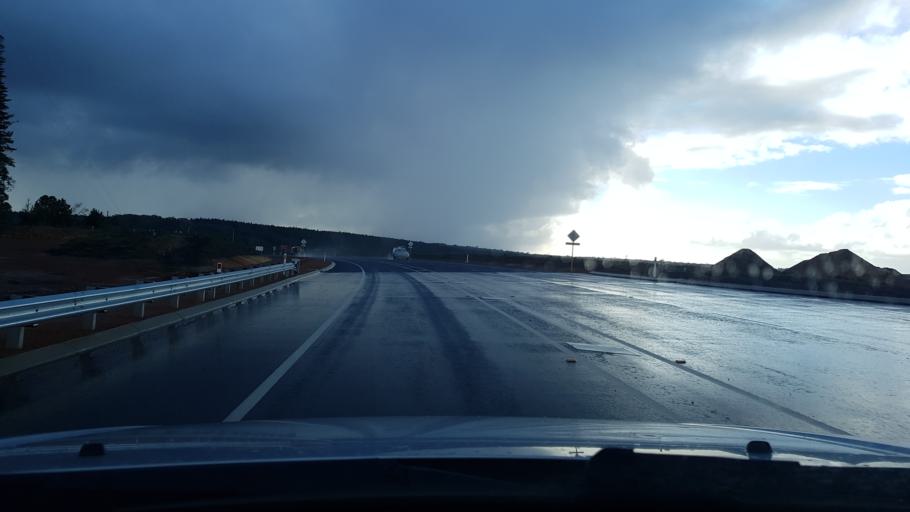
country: AU
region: Western Australia
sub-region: Augusta-Margaret River Shire
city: Margaret River
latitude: -33.9353
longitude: 115.0885
